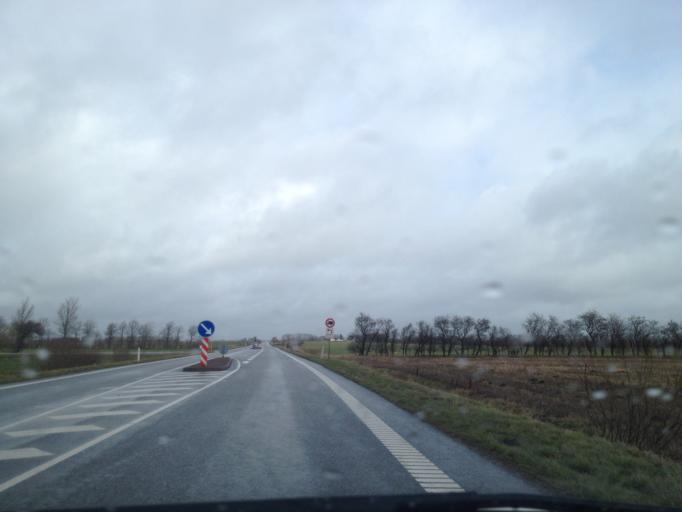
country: DK
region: South Denmark
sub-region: Tonder Kommune
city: Toftlund
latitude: 55.2074
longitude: 9.0923
